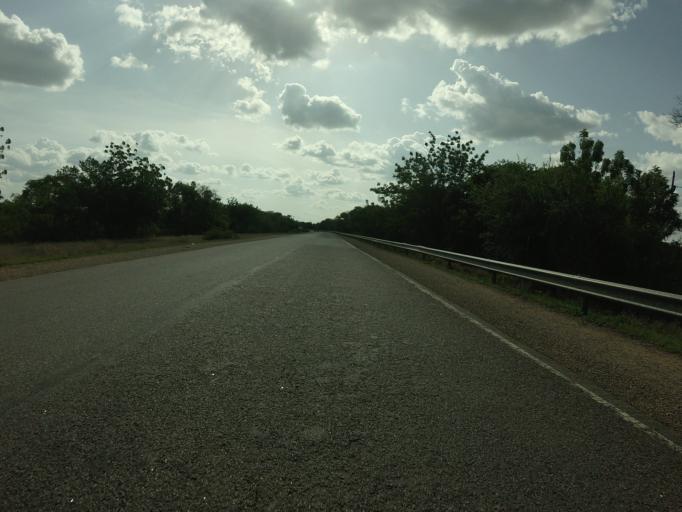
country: GH
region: Upper East
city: Bolgatanga
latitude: 10.5839
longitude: -0.8352
